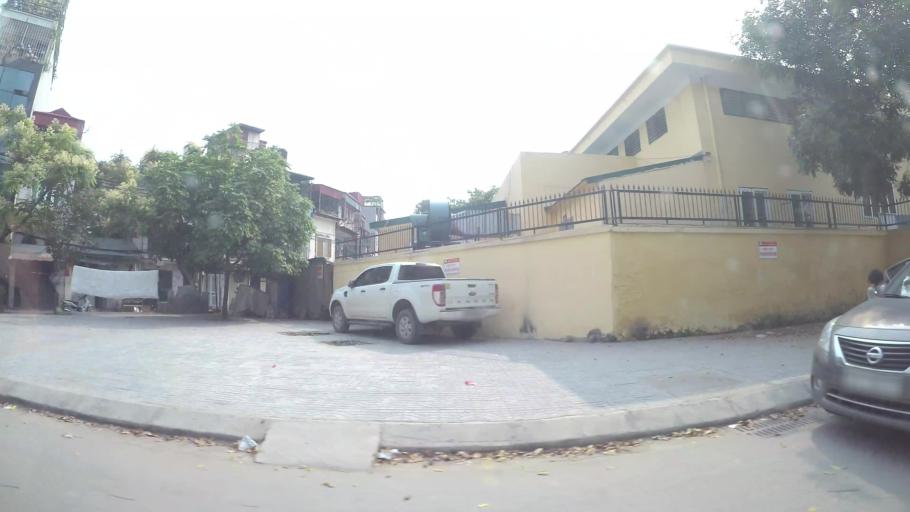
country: VN
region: Ha Noi
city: Thanh Xuan
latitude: 20.9865
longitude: 105.8019
